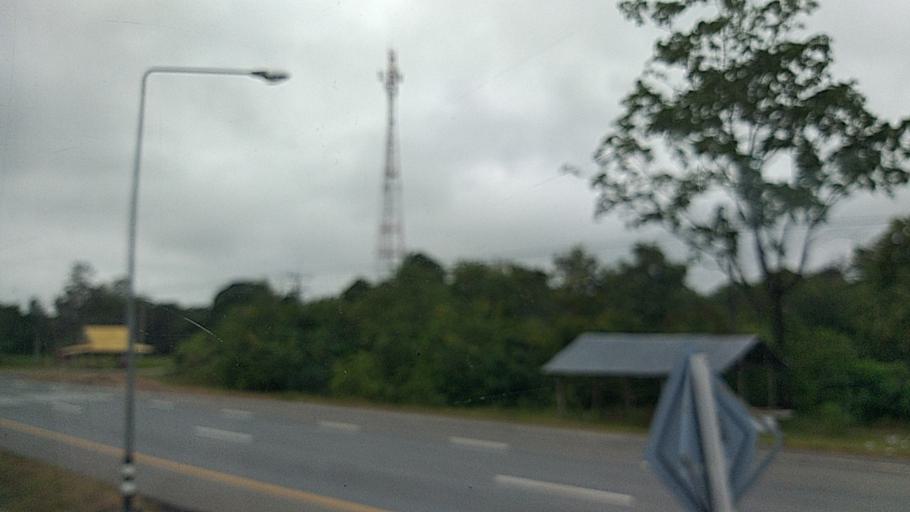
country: TH
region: Nakhon Ratchasima
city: Non Daeng
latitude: 15.4116
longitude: 102.4787
